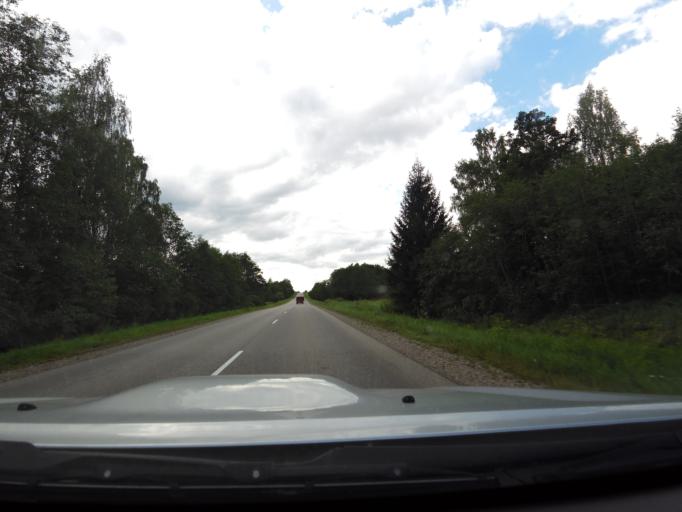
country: LV
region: Ilukste
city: Ilukste
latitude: 55.9685
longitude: 26.0353
